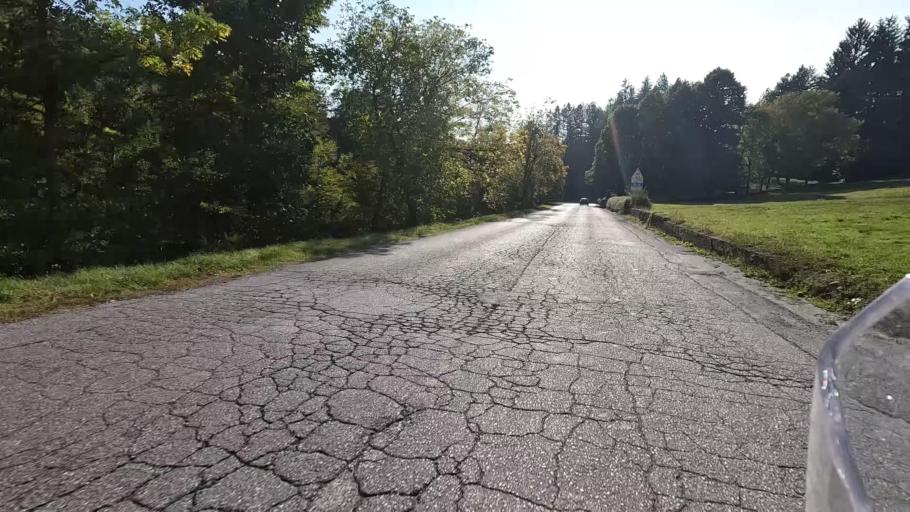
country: IT
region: Liguria
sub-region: Provincia di Savona
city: Sassello
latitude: 44.4862
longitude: 8.5048
